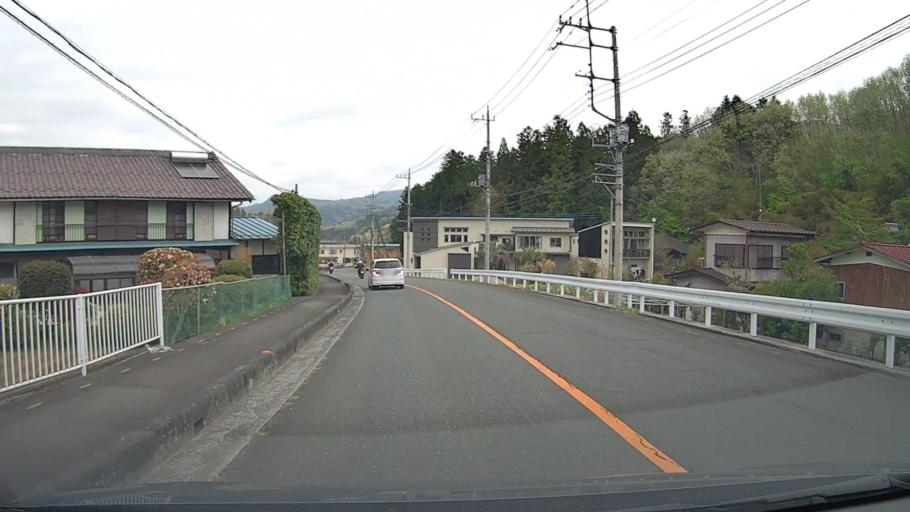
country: JP
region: Saitama
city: Chichibu
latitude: 36.0389
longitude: 139.1286
